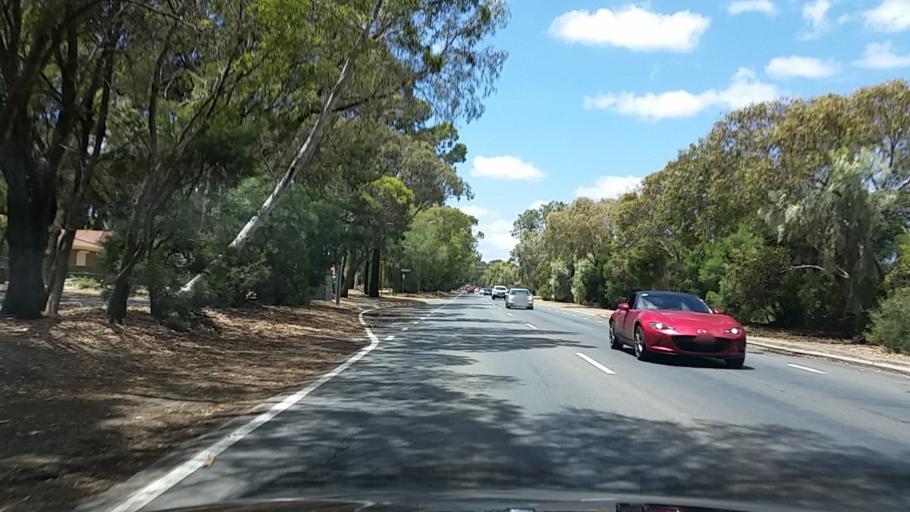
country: AU
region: South Australia
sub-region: Salisbury
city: Salisbury
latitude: -34.7644
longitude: 138.6021
